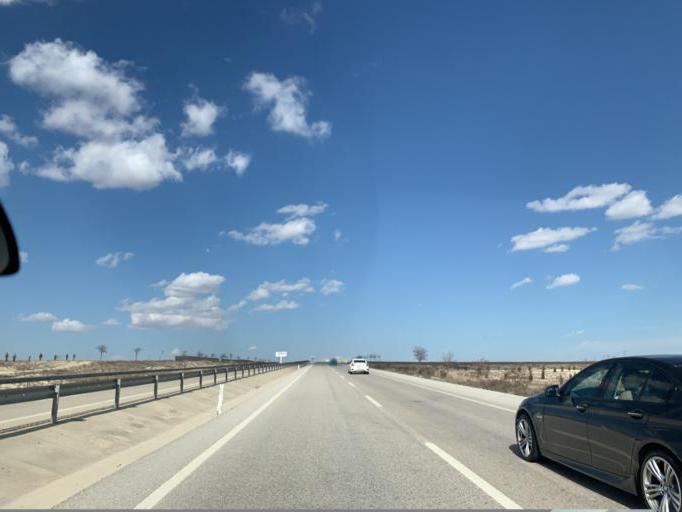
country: TR
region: Konya
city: Cihanbeyli
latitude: 38.5311
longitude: 32.8736
